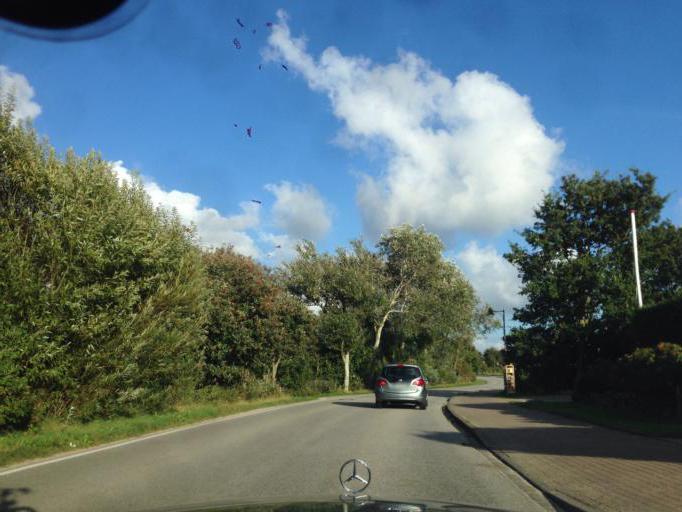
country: DE
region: Schleswig-Holstein
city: Sylt-Ost
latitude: 54.8706
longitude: 8.4343
